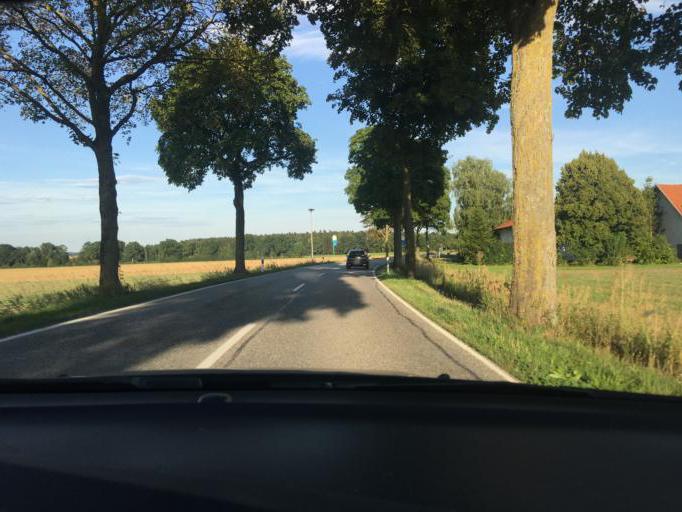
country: DE
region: Bavaria
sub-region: Upper Bavaria
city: Bockhorn
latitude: 48.2939
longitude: 11.9613
